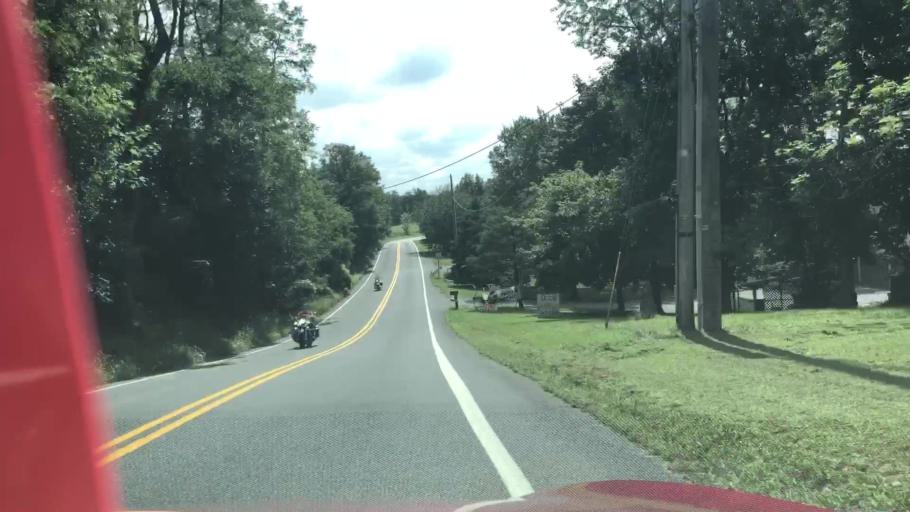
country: US
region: Pennsylvania
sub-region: Dauphin County
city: Skyline View
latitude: 40.3570
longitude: -76.6710
